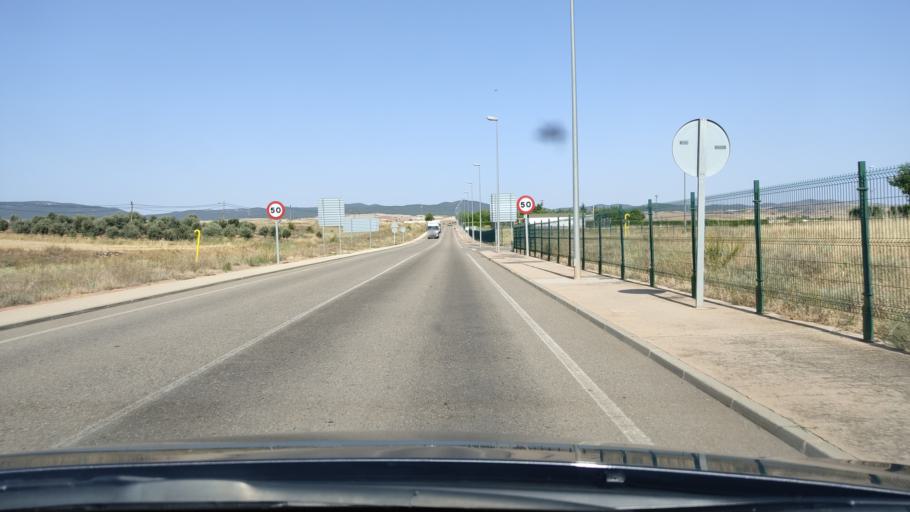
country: ES
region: Aragon
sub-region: Provincia de Teruel
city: Calamocha
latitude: 40.9179
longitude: -1.2843
